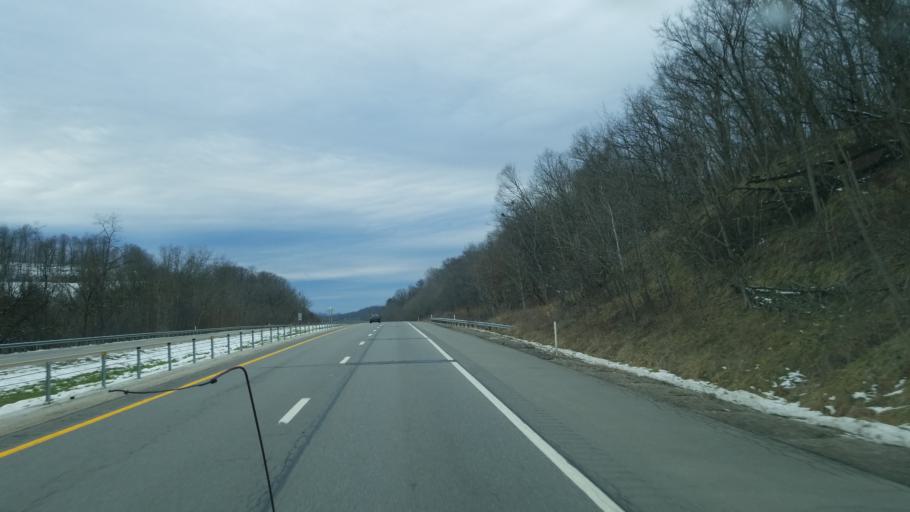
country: US
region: West Virginia
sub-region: Wood County
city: Mineral Wells
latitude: 39.0646
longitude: -81.5729
